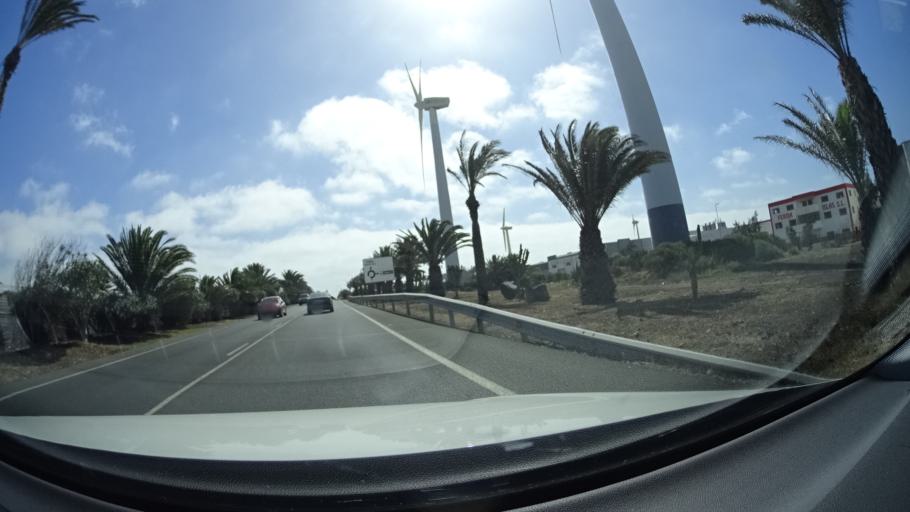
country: ES
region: Canary Islands
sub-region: Provincia de Las Palmas
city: Cruce de Arinaga
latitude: 27.8639
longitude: -15.4072
